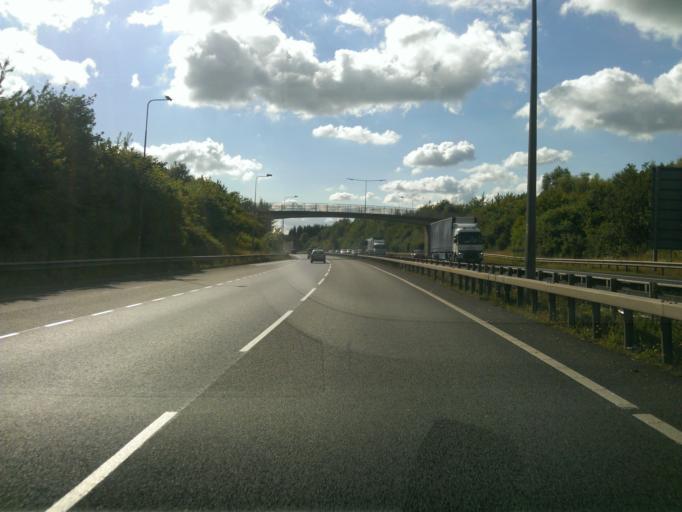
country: GB
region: England
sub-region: Staffordshire
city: Tamworth
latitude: 52.6221
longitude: -1.6779
